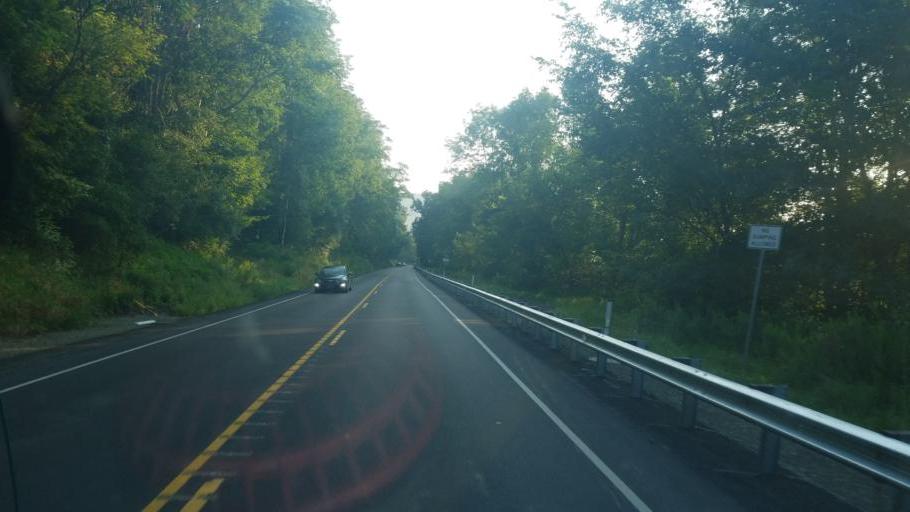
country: US
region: Pennsylvania
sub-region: Tioga County
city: Westfield
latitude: 41.9447
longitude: -77.4739
